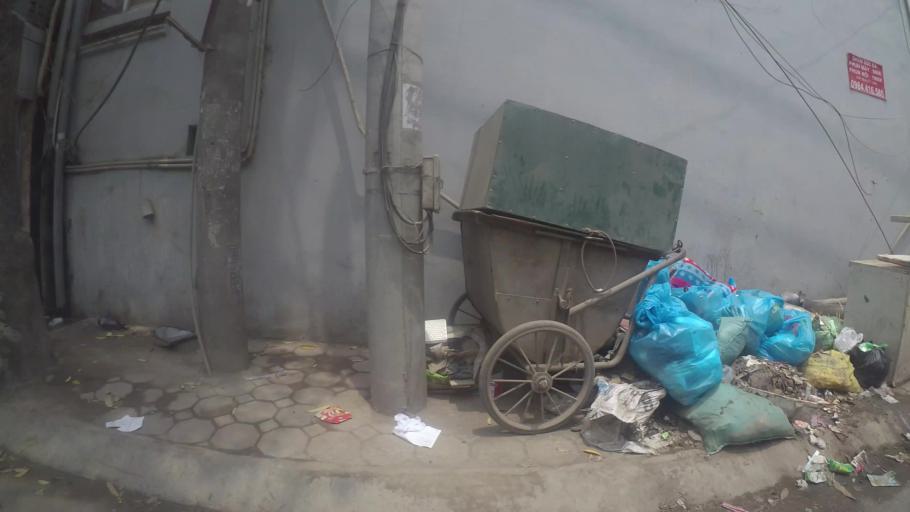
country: VN
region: Ha Noi
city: Tay Ho
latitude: 21.0790
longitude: 105.7862
